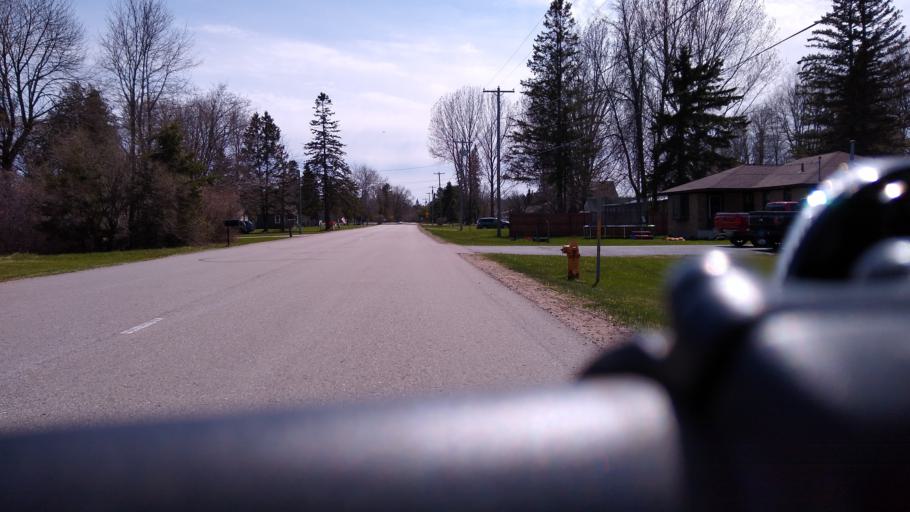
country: US
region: Michigan
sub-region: Delta County
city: Escanaba
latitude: 45.6790
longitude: -87.1451
